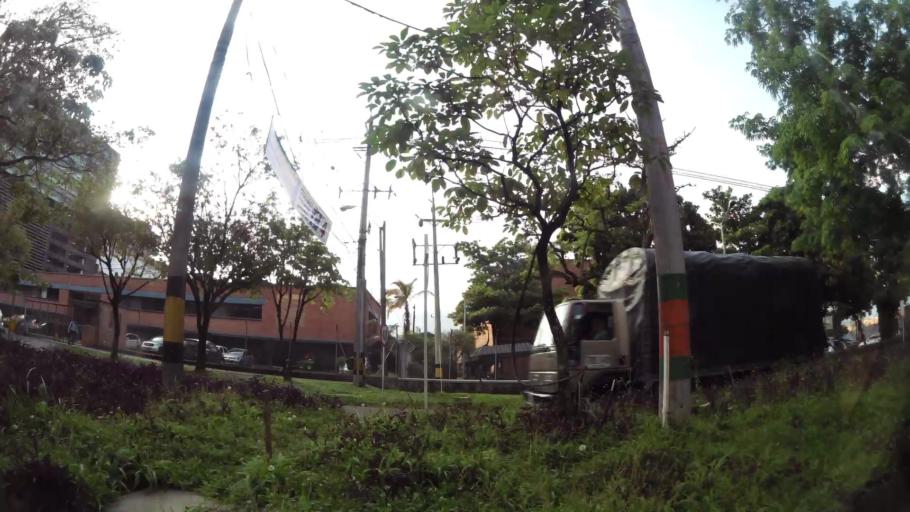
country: CO
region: Antioquia
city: Envigado
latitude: 6.1776
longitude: -75.5896
